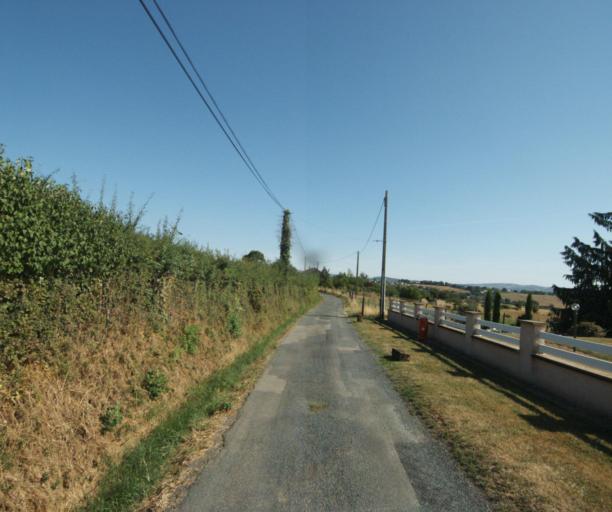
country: FR
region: Rhone-Alpes
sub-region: Departement du Rhone
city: Savigny
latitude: 45.8068
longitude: 4.5763
